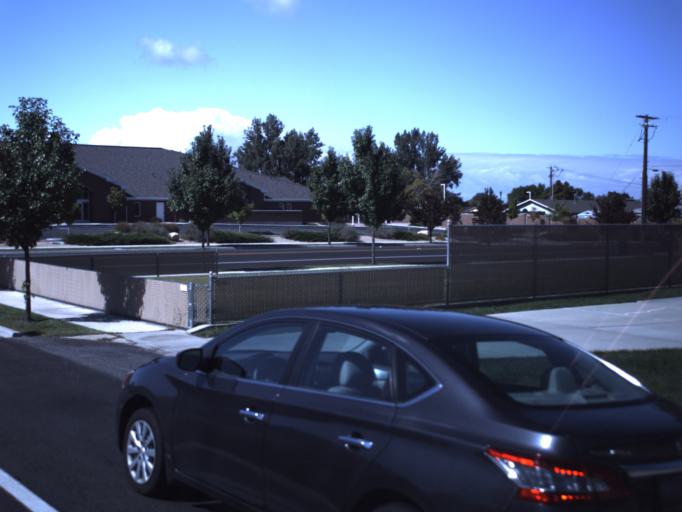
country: US
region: Utah
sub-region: Utah County
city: Spanish Fork
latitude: 40.1150
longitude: -111.6473
